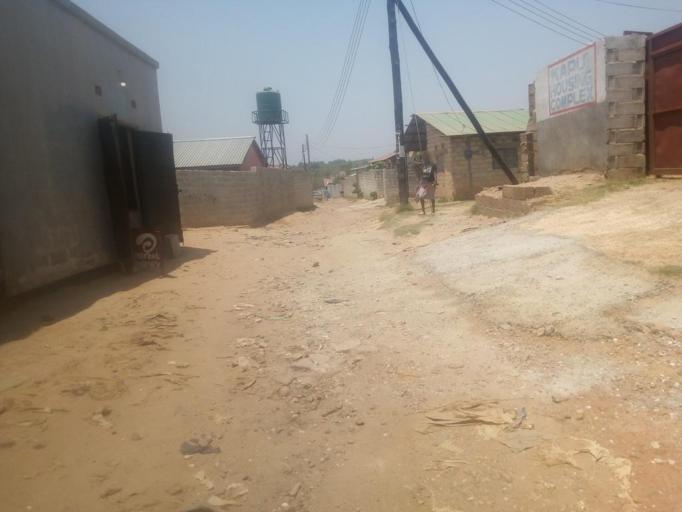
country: ZM
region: Lusaka
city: Lusaka
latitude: -15.4079
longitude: 28.3747
